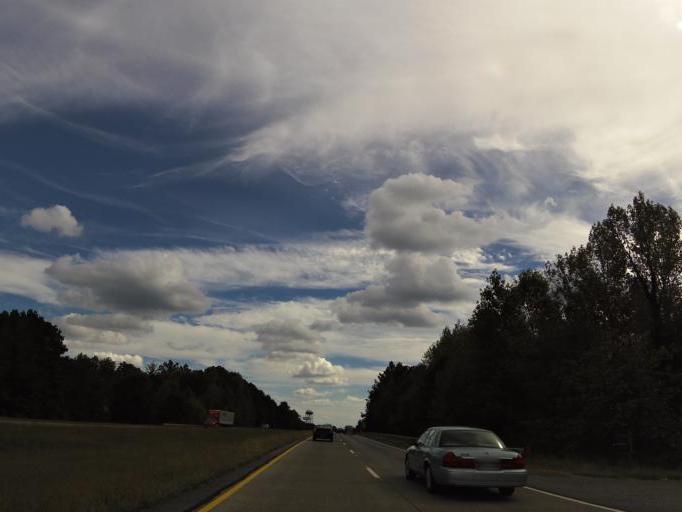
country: US
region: Georgia
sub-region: Pickens County
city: Jasper
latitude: 34.4347
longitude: -84.4361
